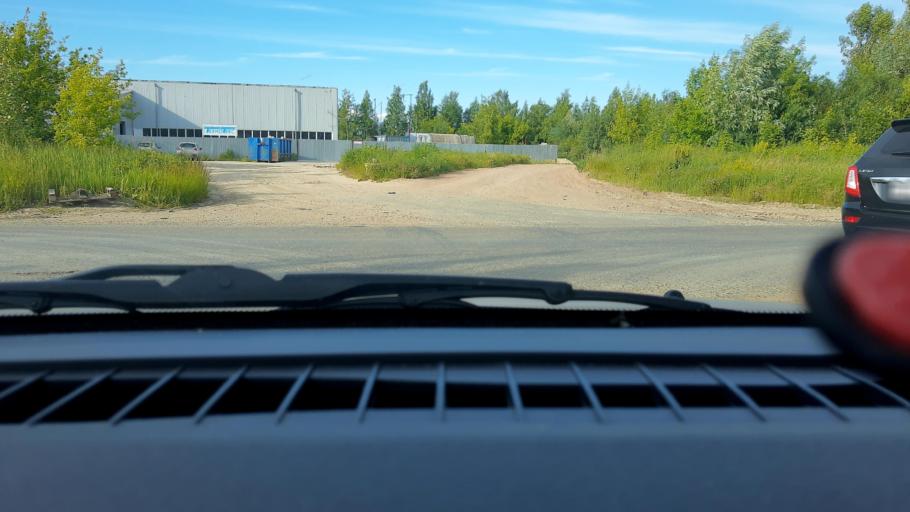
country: RU
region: Nizjnij Novgorod
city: Kstovo
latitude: 56.1252
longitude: 44.1389
